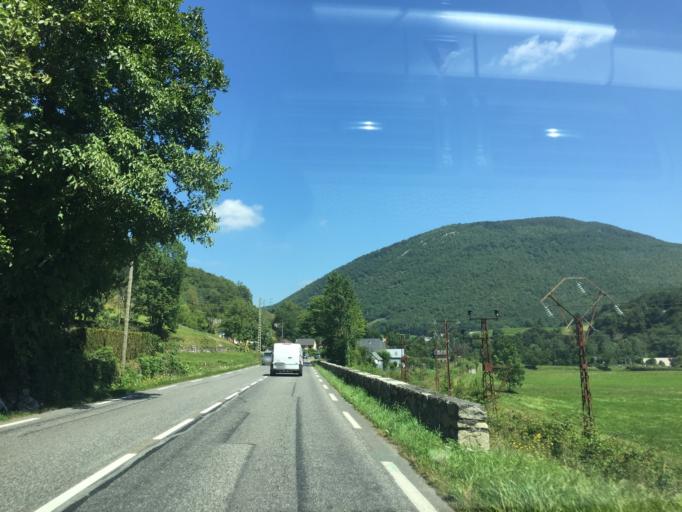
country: FR
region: Midi-Pyrenees
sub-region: Departement des Hautes-Pyrenees
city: La Barthe-de-Neste
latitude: 42.9985
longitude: 0.3738
